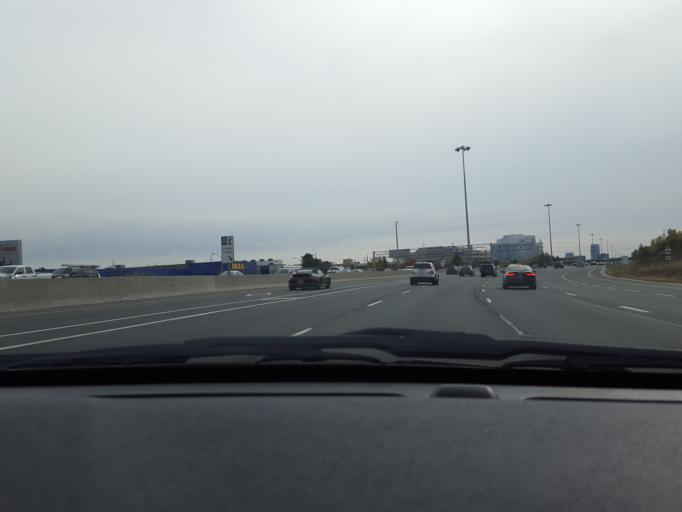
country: CA
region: Ontario
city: Willowdale
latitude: 43.8100
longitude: -79.3474
